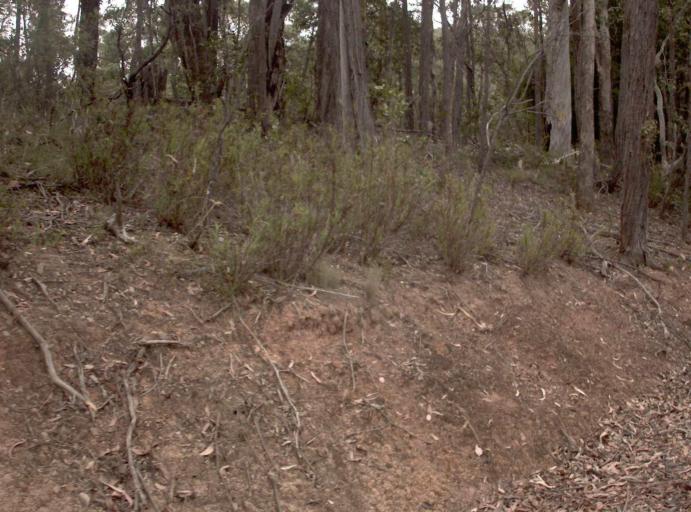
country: AU
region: Victoria
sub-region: East Gippsland
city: Bairnsdale
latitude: -37.6931
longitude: 147.2943
